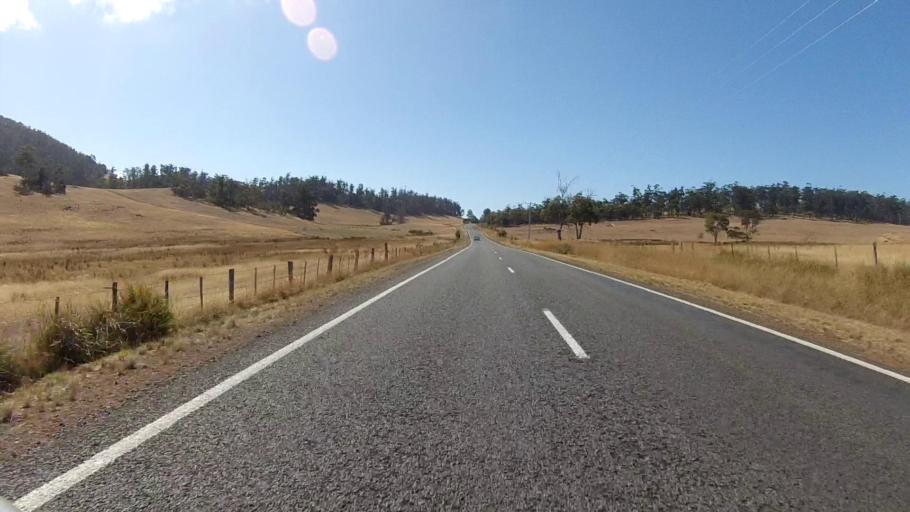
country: AU
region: Tasmania
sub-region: Sorell
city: Sorell
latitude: -42.4345
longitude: 147.9307
